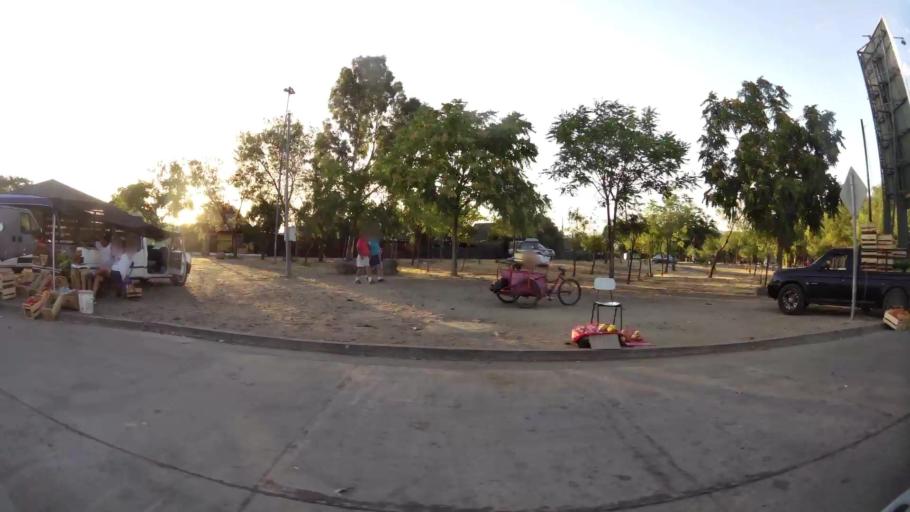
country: CL
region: Maule
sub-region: Provincia de Talca
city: Talca
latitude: -35.4461
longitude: -71.6689
